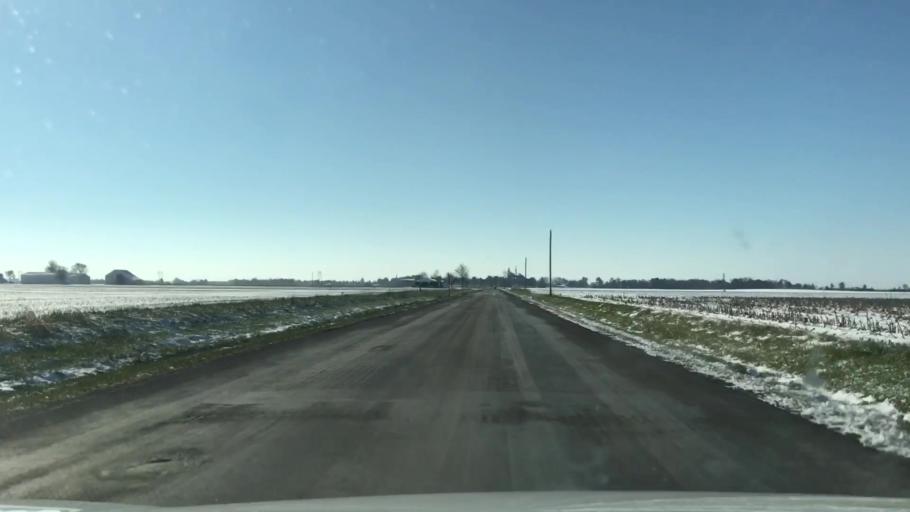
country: US
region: Illinois
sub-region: Washington County
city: Okawville
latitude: 38.4102
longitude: -89.4866
